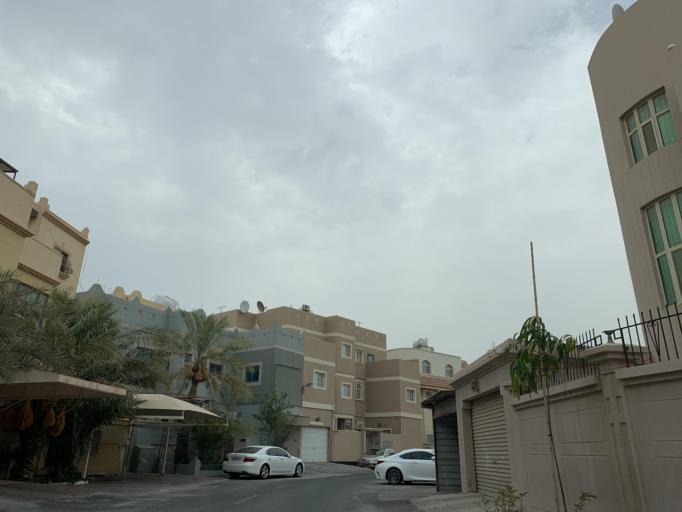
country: BH
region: Northern
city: Madinat `Isa
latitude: 26.1855
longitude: 50.4778
